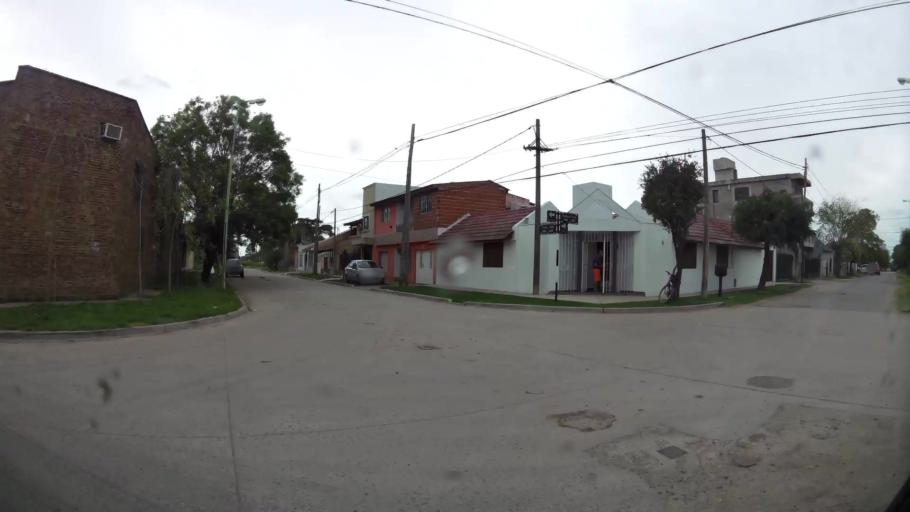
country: AR
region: Buenos Aires
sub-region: Partido de Zarate
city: Zarate
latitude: -34.1189
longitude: -59.0207
